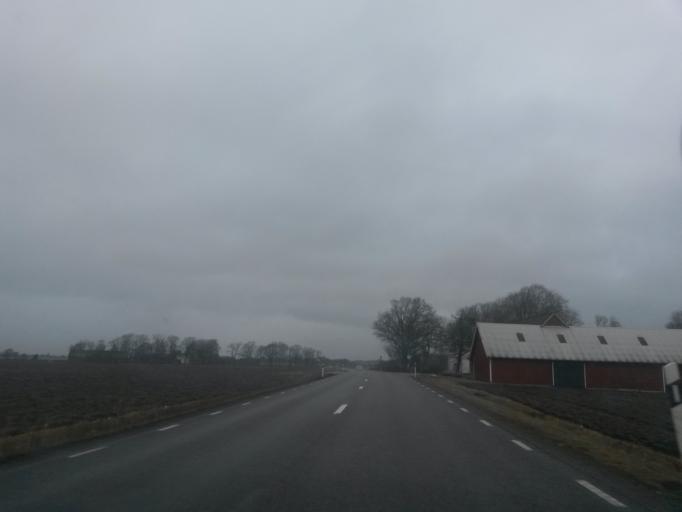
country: SE
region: Vaestra Goetaland
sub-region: Vanersborgs Kommun
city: Vargon
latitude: 58.2757
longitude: 12.3991
